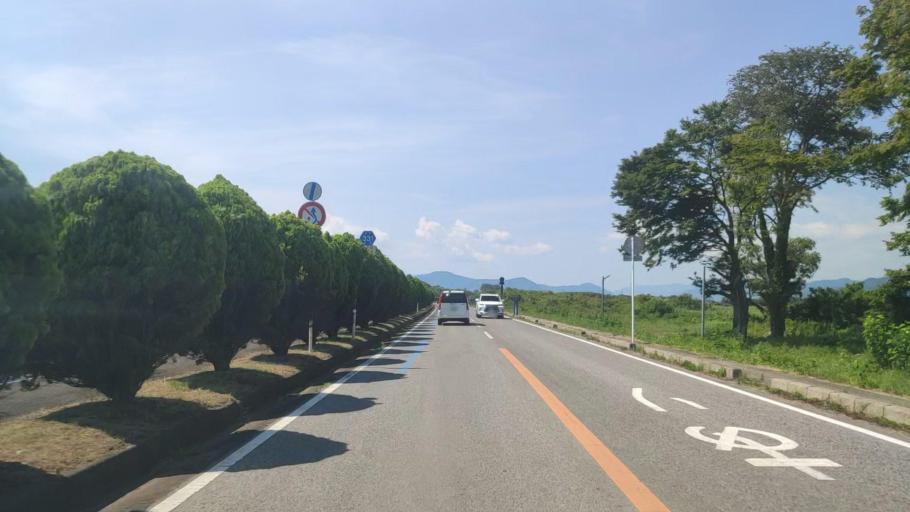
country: JP
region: Shiga Prefecture
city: Nagahama
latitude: 35.4147
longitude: 136.2039
